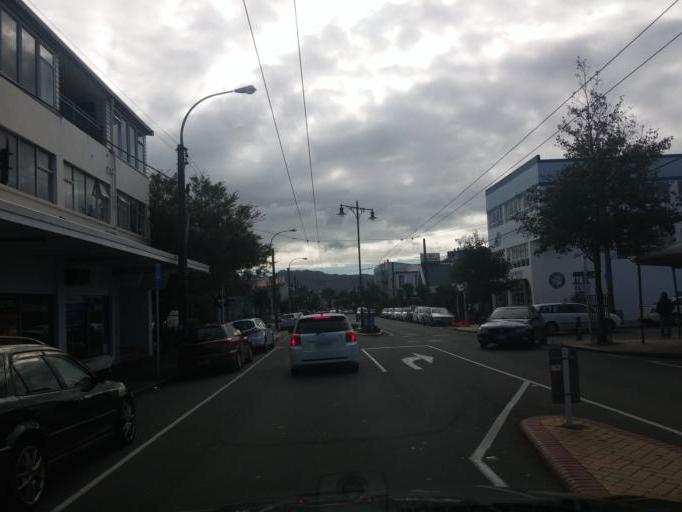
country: NZ
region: Wellington
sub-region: Wellington City
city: Wellington
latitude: -41.3151
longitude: 174.7802
